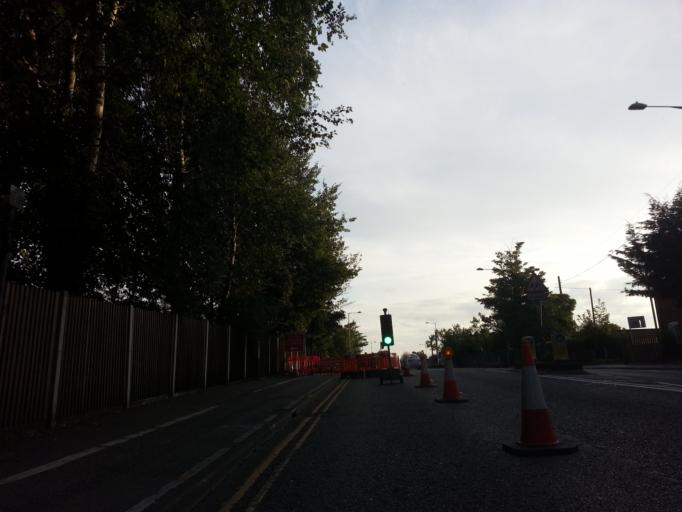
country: GB
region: England
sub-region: Suffolk
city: Ipswich
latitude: 52.0569
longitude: 1.1316
